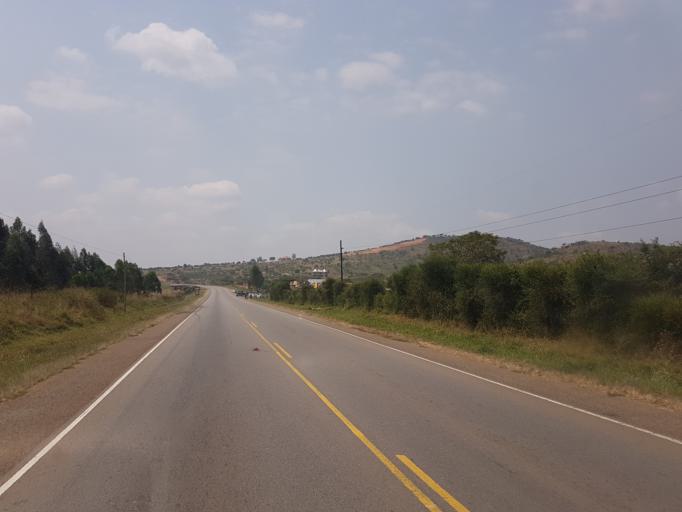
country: UG
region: Western Region
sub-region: Mbarara District
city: Mbarara
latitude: -0.5037
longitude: 30.8479
